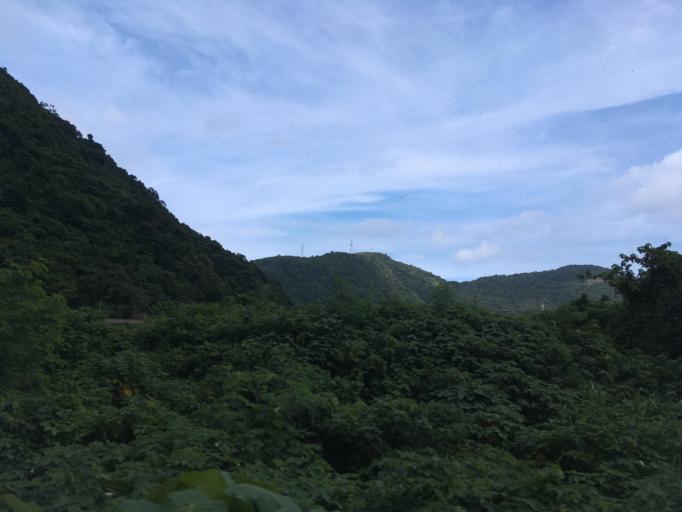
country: TW
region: Taiwan
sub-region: Yilan
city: Yilan
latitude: 24.4432
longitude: 121.7670
